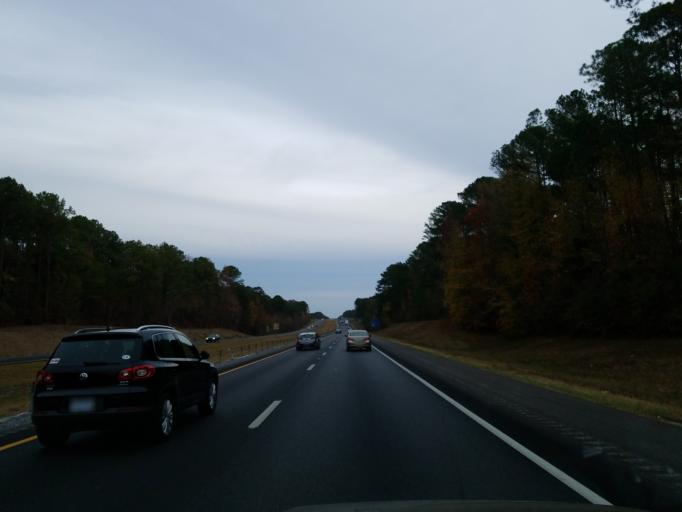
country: US
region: Mississippi
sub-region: Lauderdale County
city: Marion
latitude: 32.3919
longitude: -88.5923
